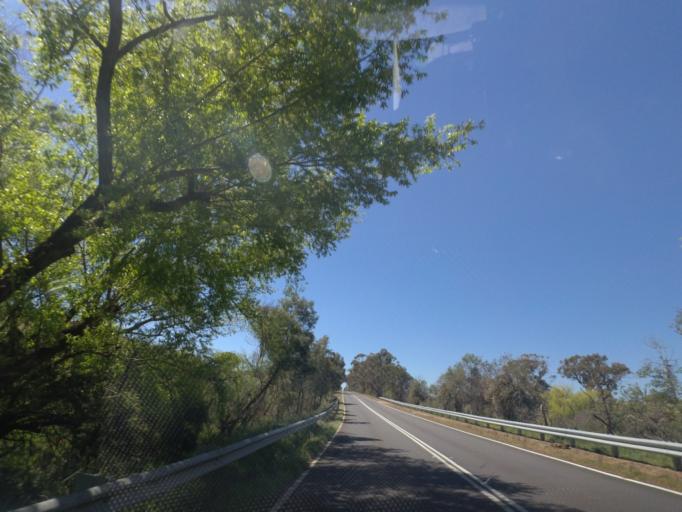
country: AU
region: Victoria
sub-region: Hume
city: Sunbury
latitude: -37.1651
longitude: 144.7604
